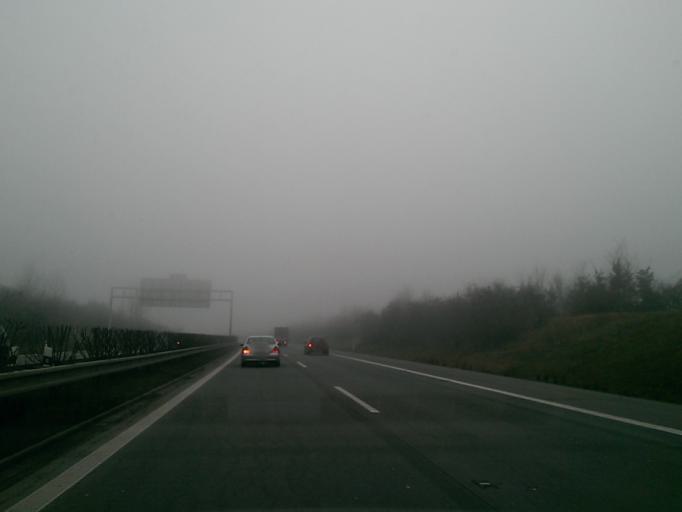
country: CZ
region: Olomoucky
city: Hnevotin
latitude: 49.5580
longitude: 17.2237
